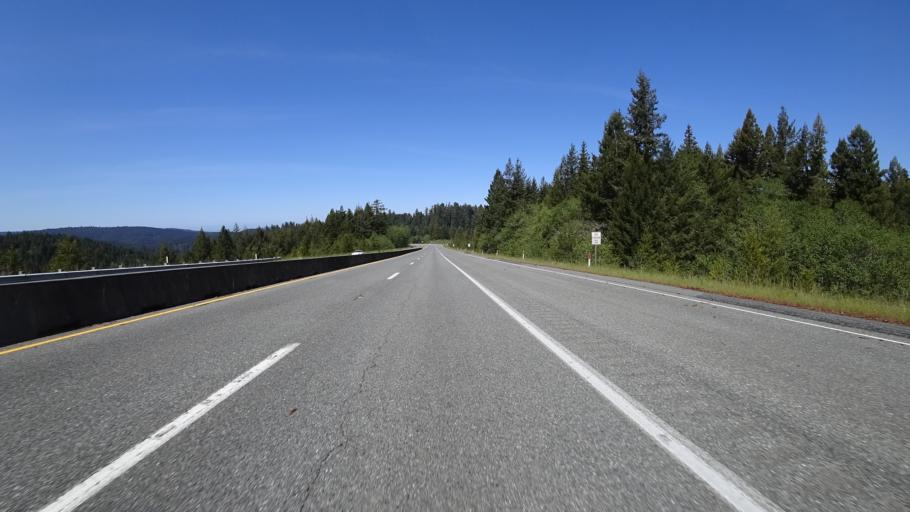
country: US
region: California
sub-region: Humboldt County
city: Westhaven-Moonstone
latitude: 41.3587
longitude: -123.9966
